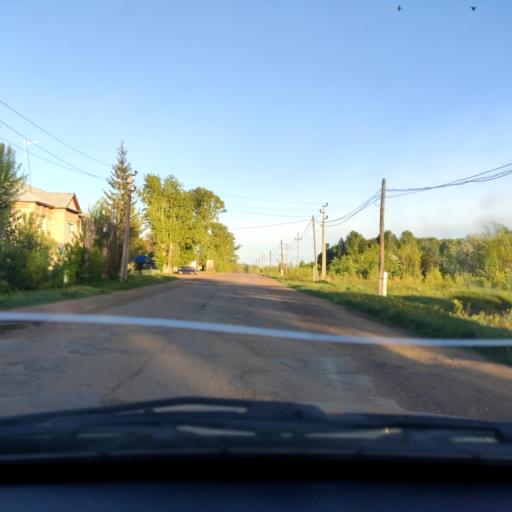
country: RU
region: Bashkortostan
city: Yazykovo
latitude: 55.0444
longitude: 56.1841
